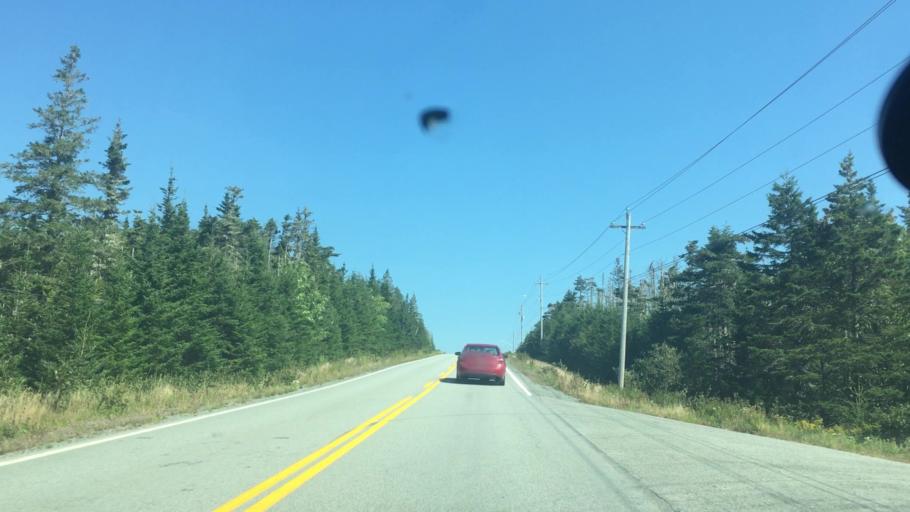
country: CA
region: Nova Scotia
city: Antigonish
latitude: 44.9374
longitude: -62.2695
